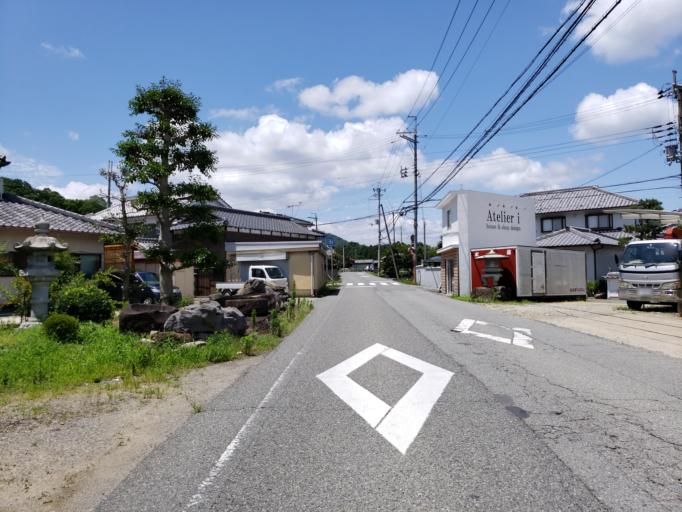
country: JP
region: Hyogo
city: Himeji
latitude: 34.9358
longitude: 134.7222
